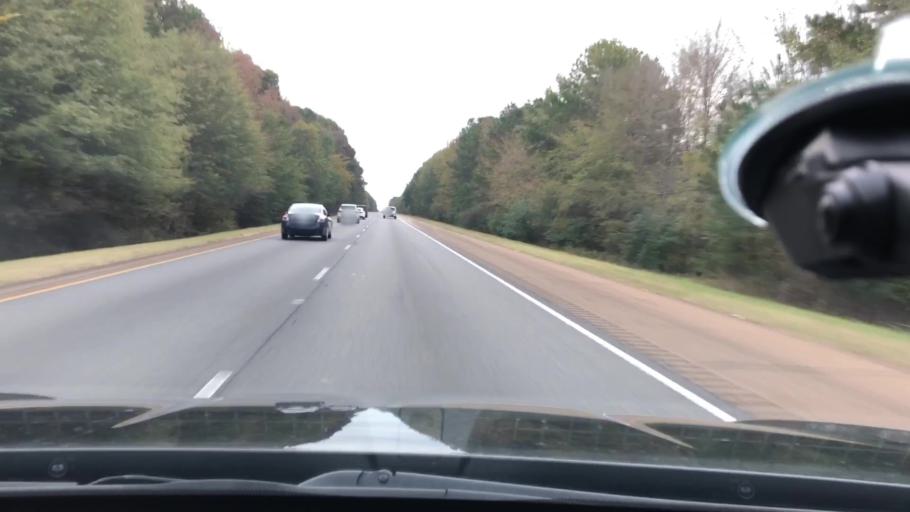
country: US
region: Arkansas
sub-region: Nevada County
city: Prescott
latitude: 33.8568
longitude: -93.3598
